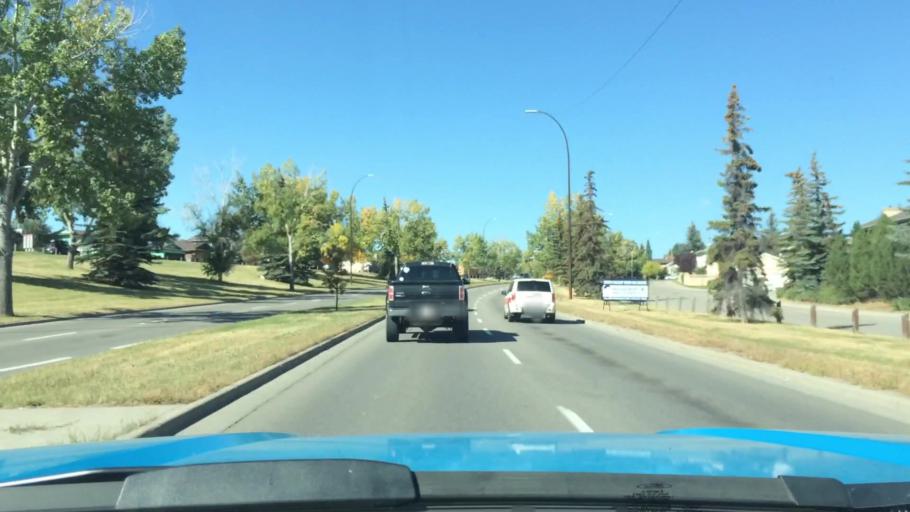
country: CA
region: Alberta
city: Calgary
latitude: 50.9131
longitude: -114.0753
